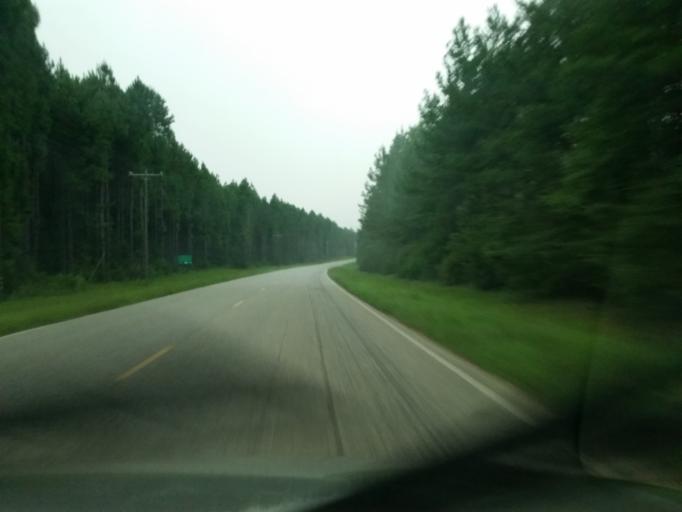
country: US
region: Florida
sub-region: Escambia County
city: Cantonment
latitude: 30.6922
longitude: -87.5083
